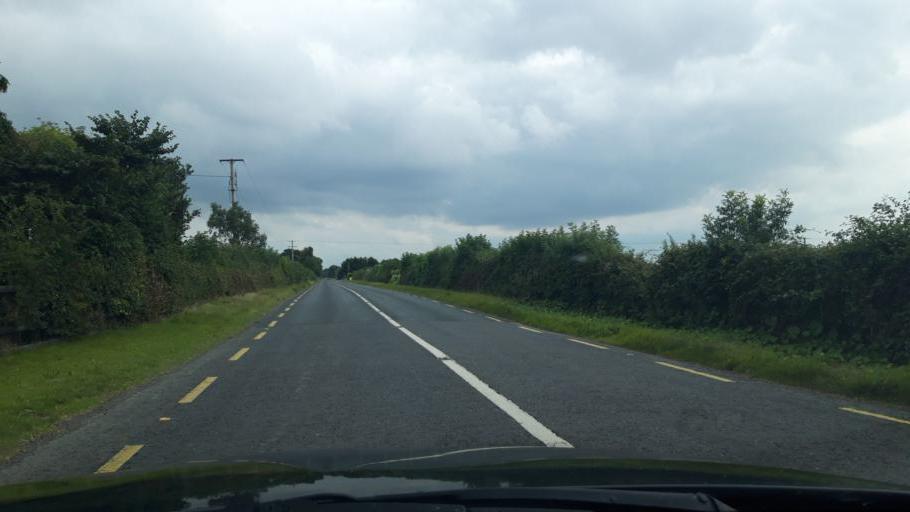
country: IE
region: Leinster
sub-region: Kildare
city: Athy
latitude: 53.0219
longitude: -7.0063
